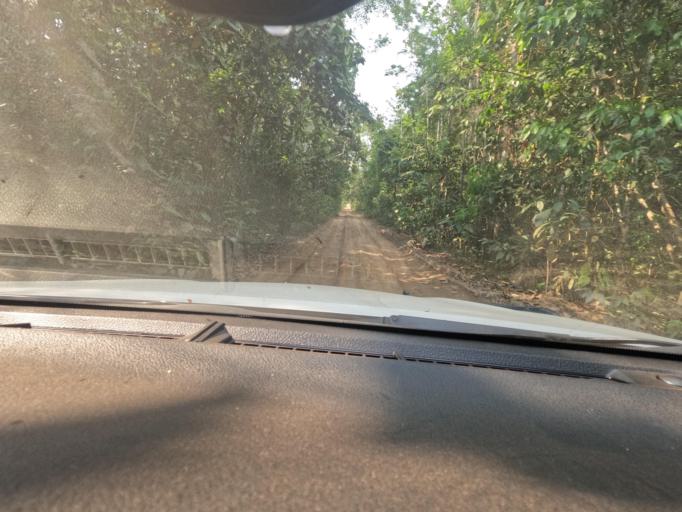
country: BR
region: Rondonia
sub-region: Porto Velho
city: Porto Velho
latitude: -8.6662
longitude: -63.1559
